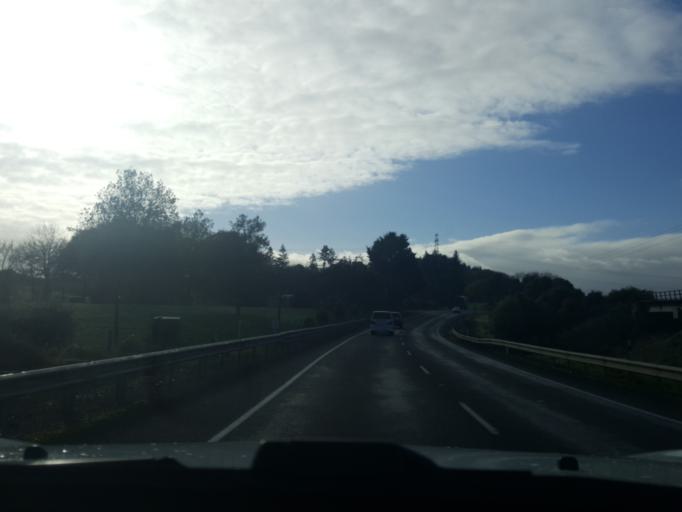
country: NZ
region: Waikato
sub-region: Waipa District
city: Cambridge
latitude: -37.6657
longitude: 175.4985
